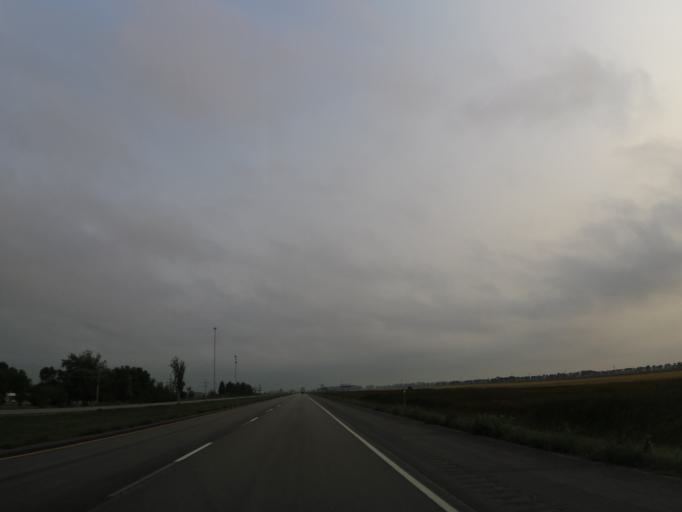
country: US
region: North Dakota
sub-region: Walsh County
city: Grafton
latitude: 48.5630
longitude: -97.1866
